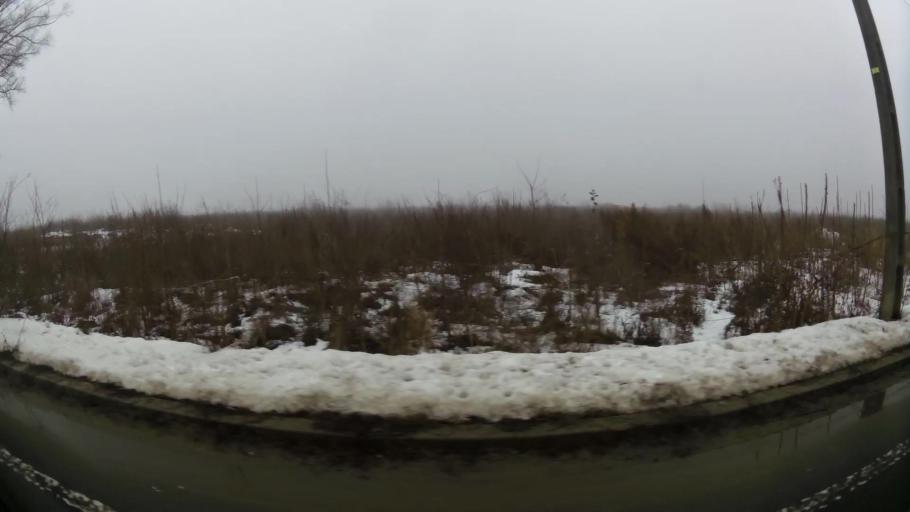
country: RO
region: Ilfov
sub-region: Comuna Chiajna
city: Chiajna
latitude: 44.4590
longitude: 25.9907
